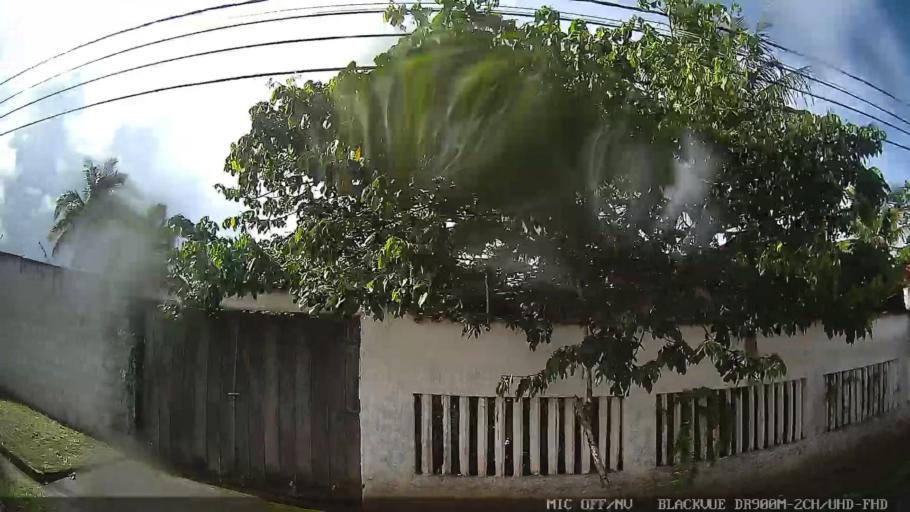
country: BR
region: Sao Paulo
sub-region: Itanhaem
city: Itanhaem
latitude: -24.2369
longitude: -46.8847
